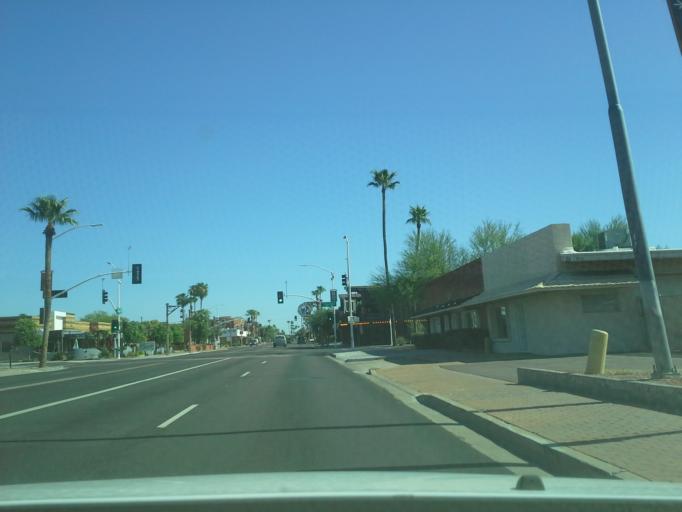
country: US
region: Arizona
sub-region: Maricopa County
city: Scottsdale
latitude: 33.4907
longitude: -111.9261
